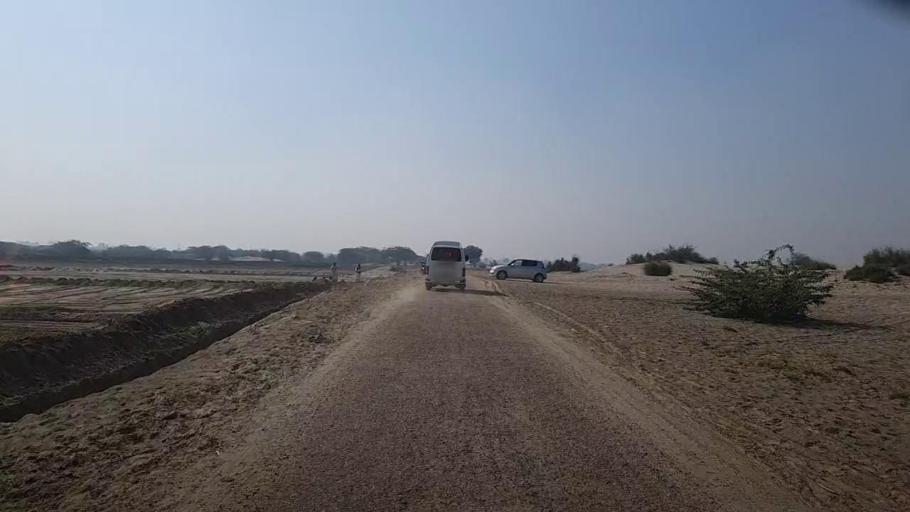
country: PK
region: Sindh
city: Bozdar
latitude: 27.2566
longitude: 68.6156
